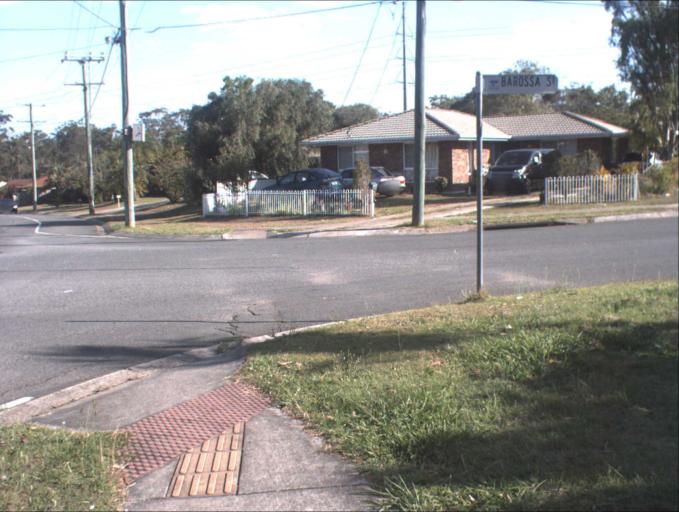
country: AU
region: Queensland
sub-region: Logan
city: Logan City
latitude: -27.6614
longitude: 153.0982
